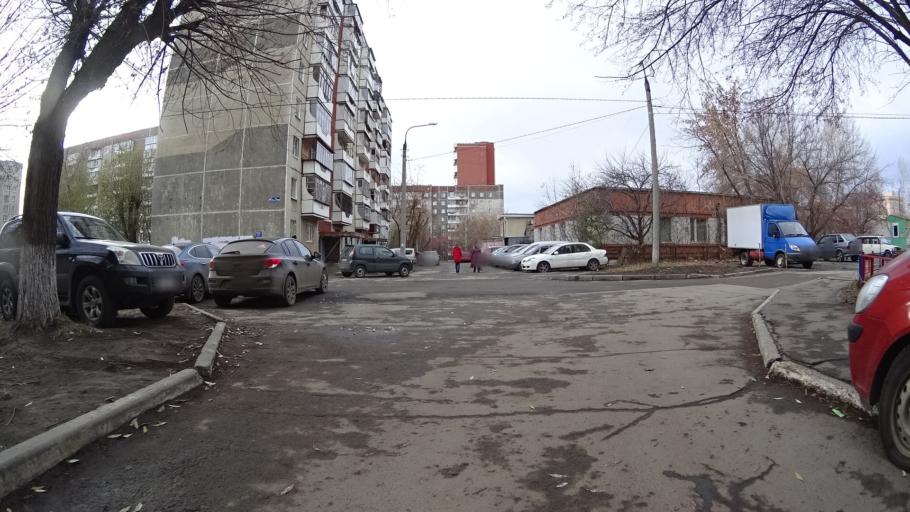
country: RU
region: Chelyabinsk
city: Roshchino
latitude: 55.1870
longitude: 61.2959
